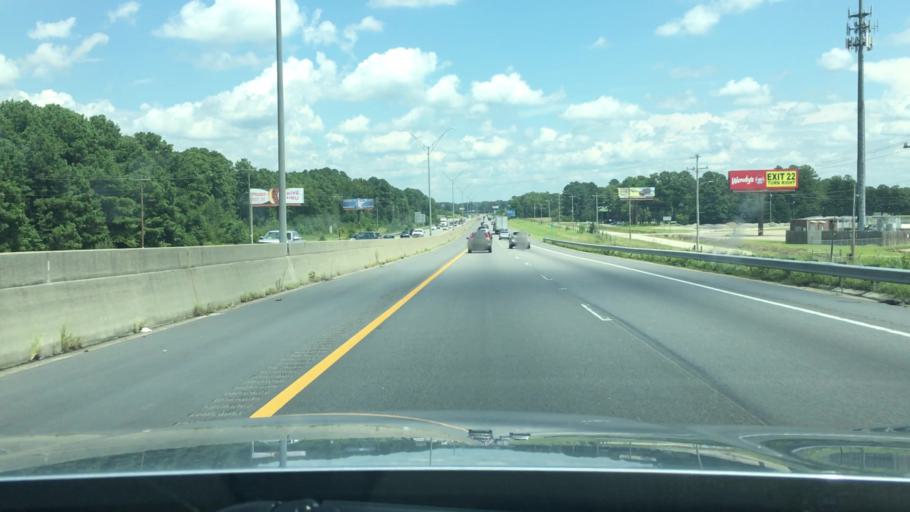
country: US
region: North Carolina
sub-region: Robeson County
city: Lumberton
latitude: 34.6284
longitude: -79.0377
